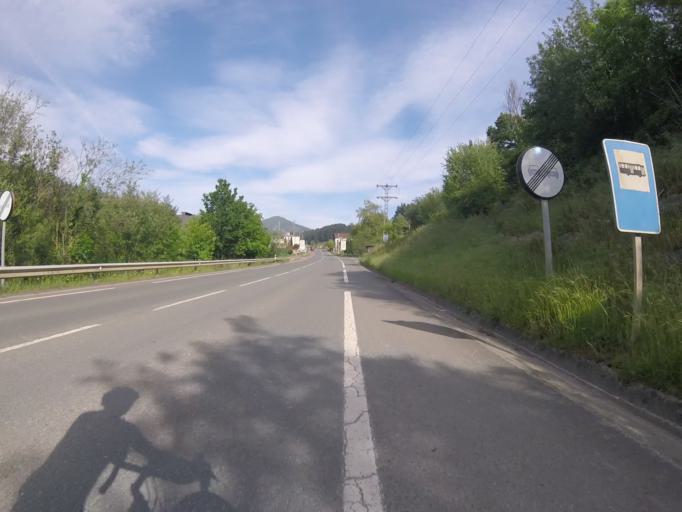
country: ES
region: Basque Country
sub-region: Provincia de Guipuzcoa
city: Zumarraga
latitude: 43.0767
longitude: -2.2919
